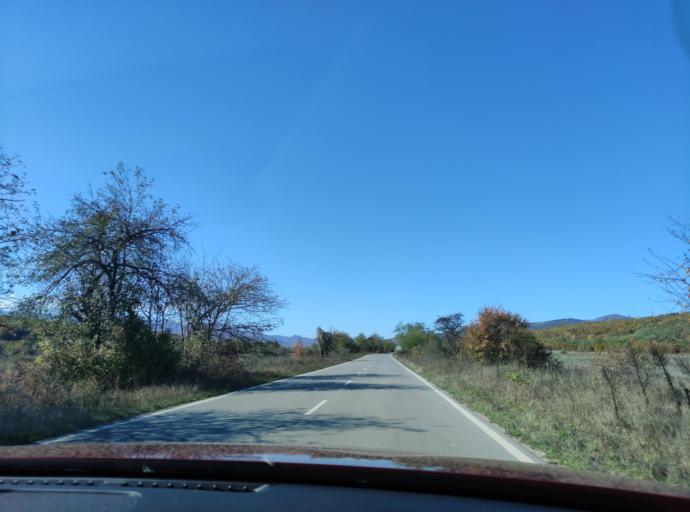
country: BG
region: Montana
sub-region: Obshtina Chiprovtsi
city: Chiprovtsi
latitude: 43.4108
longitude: 23.0466
